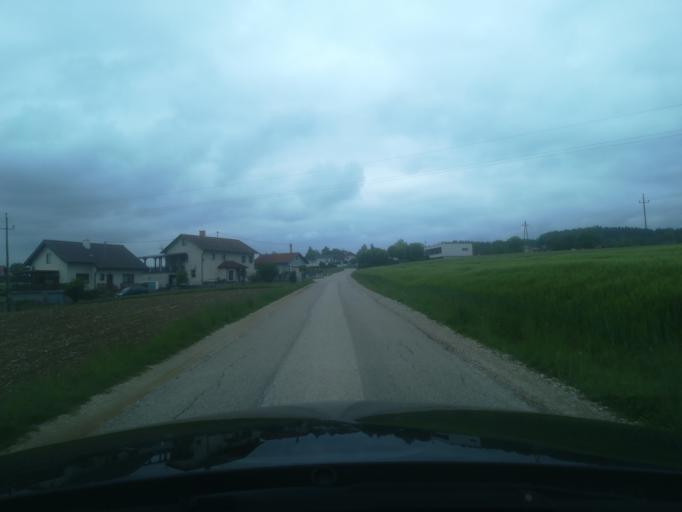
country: AT
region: Upper Austria
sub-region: Wels-Land
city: Holzhausen
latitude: 48.2368
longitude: 14.0740
